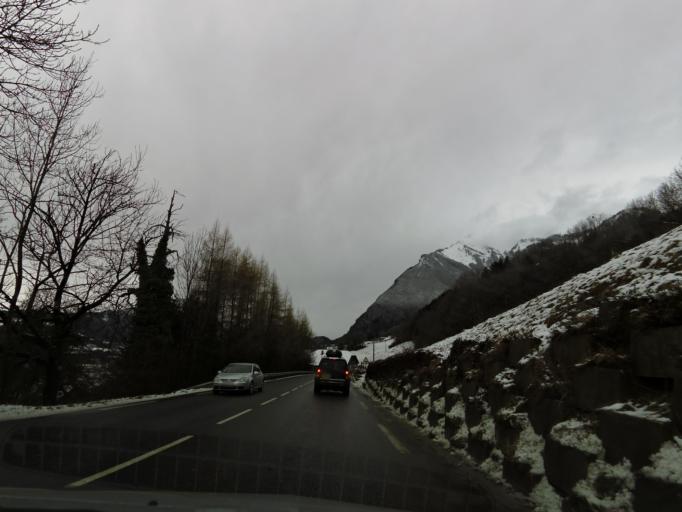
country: FR
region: Rhone-Alpes
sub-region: Departement de la Haute-Savoie
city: Taninges
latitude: 46.1096
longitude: 6.6140
